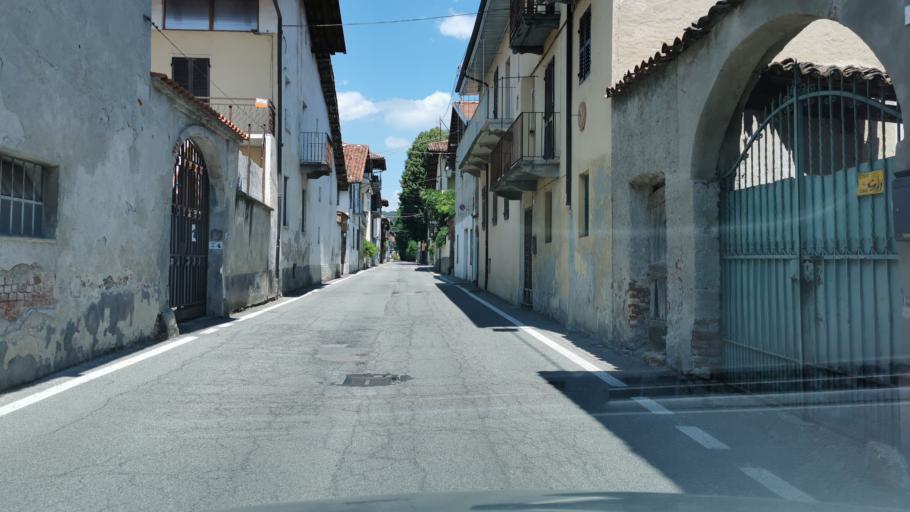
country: IT
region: Piedmont
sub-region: Provincia di Torino
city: Aglie
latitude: 45.3662
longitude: 7.7684
